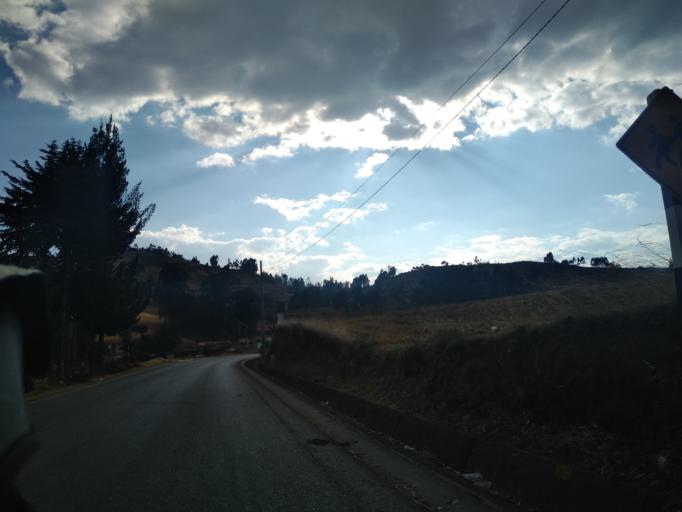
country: PE
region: Cajamarca
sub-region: Provincia de Cajamarca
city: Llacanora
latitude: -7.1435
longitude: -78.4085
